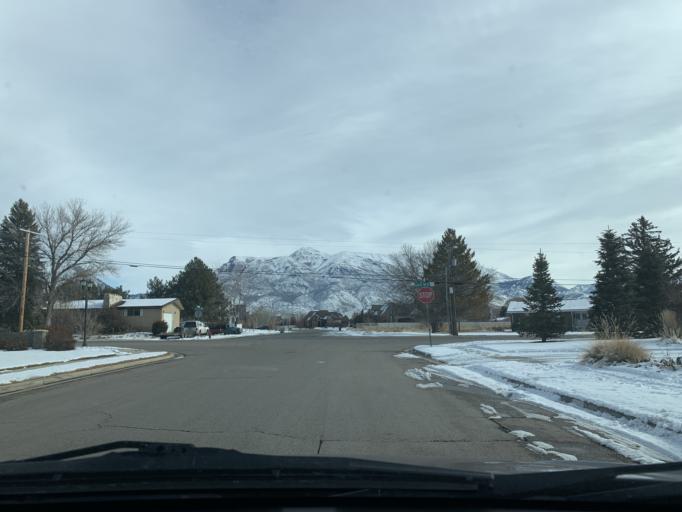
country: US
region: Utah
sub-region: Utah County
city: Lehi
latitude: 40.4118
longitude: -111.8214
